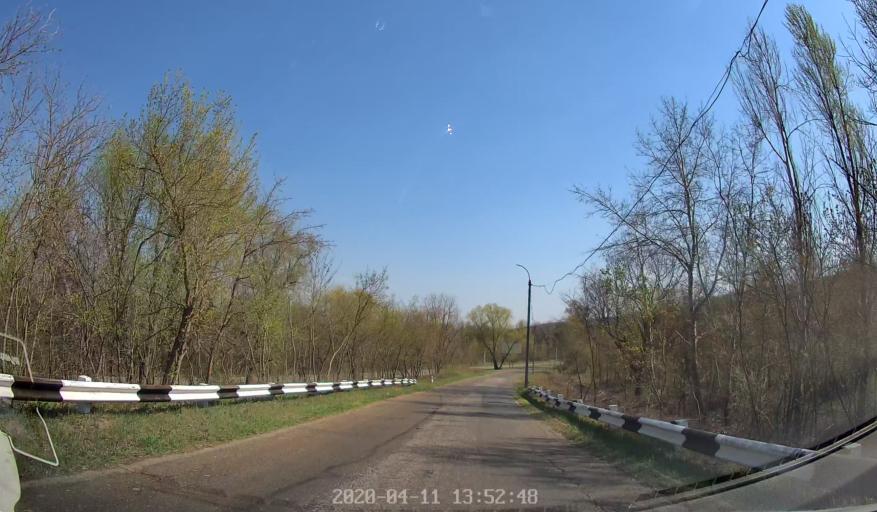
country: MD
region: Chisinau
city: Vadul lui Voda
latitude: 47.0825
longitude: 29.0903
